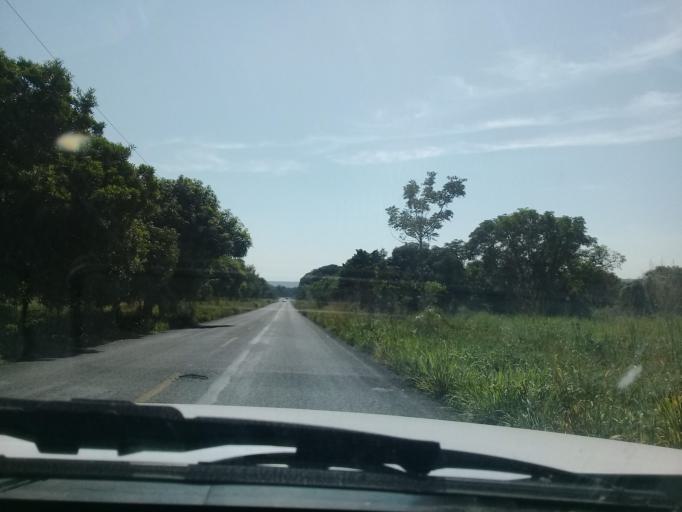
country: MX
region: Veracruz
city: Actopan
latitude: 19.4665
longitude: -96.5756
